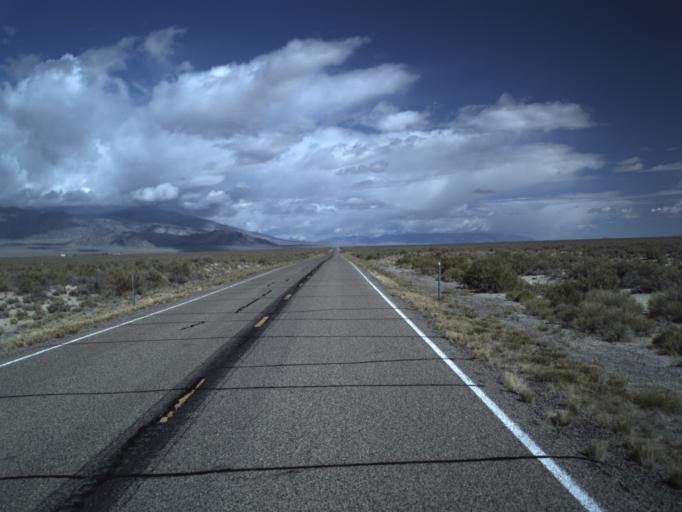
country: US
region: Nevada
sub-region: White Pine County
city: McGill
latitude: 39.0178
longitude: -114.0353
